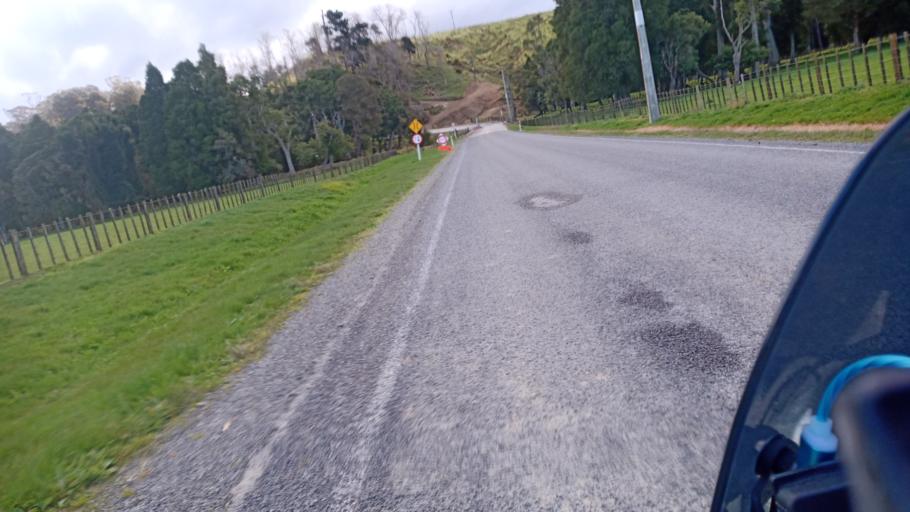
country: NZ
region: Gisborne
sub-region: Gisborne District
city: Gisborne
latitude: -38.3323
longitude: 178.2547
